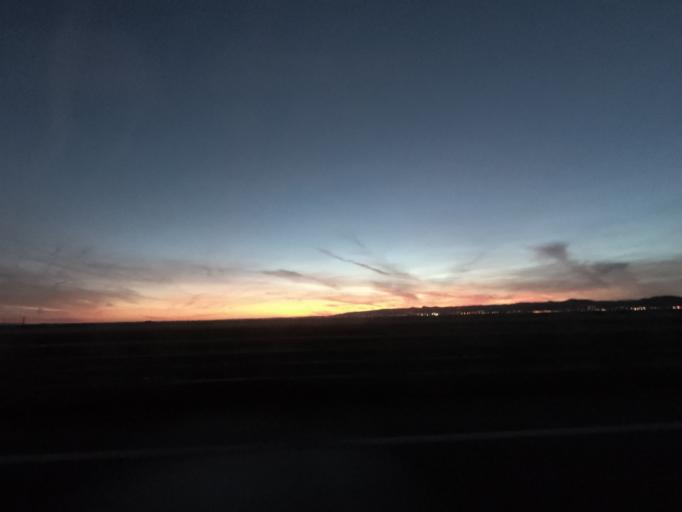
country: PT
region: Lisbon
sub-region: Vila Franca de Xira
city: Castanheira do Ribatejo
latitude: 39.0000
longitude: -8.9045
